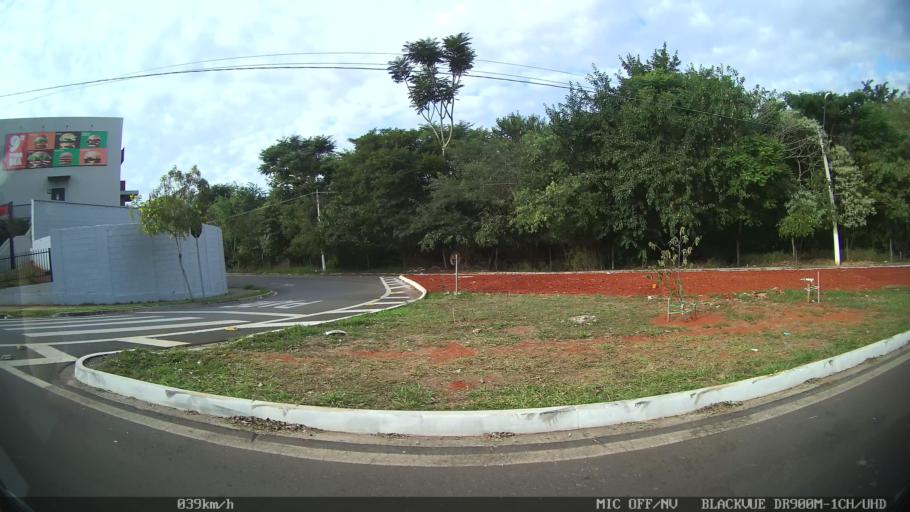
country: BR
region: Sao Paulo
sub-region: Santa Barbara D'Oeste
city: Santa Barbara d'Oeste
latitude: -22.7501
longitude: -47.3765
